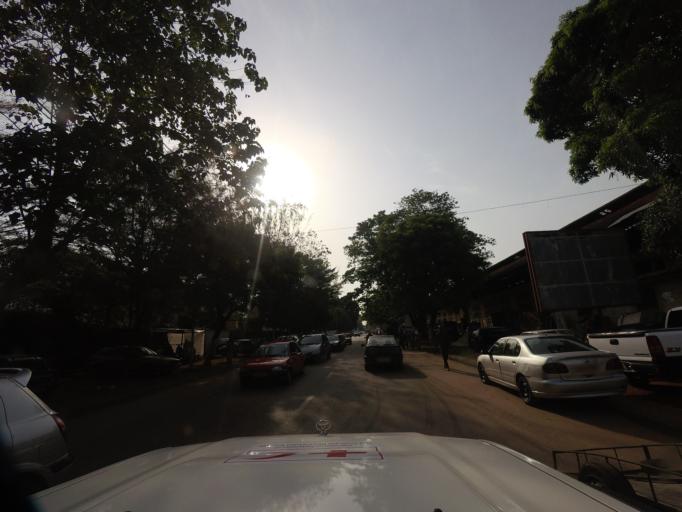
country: GN
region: Conakry
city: Camayenne
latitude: 9.5134
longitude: -13.7056
